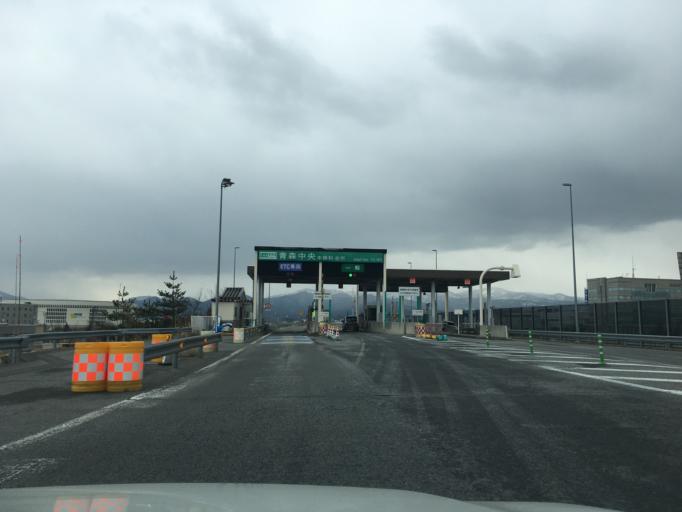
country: JP
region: Aomori
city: Aomori Shi
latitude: 40.7962
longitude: 140.7448
